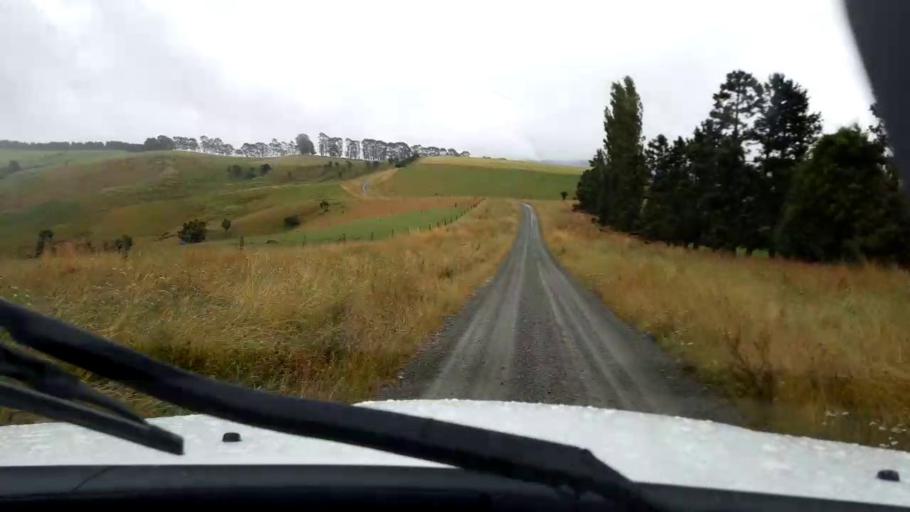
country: NZ
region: Canterbury
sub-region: Timaru District
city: Pleasant Point
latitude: -44.1759
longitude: 171.1143
